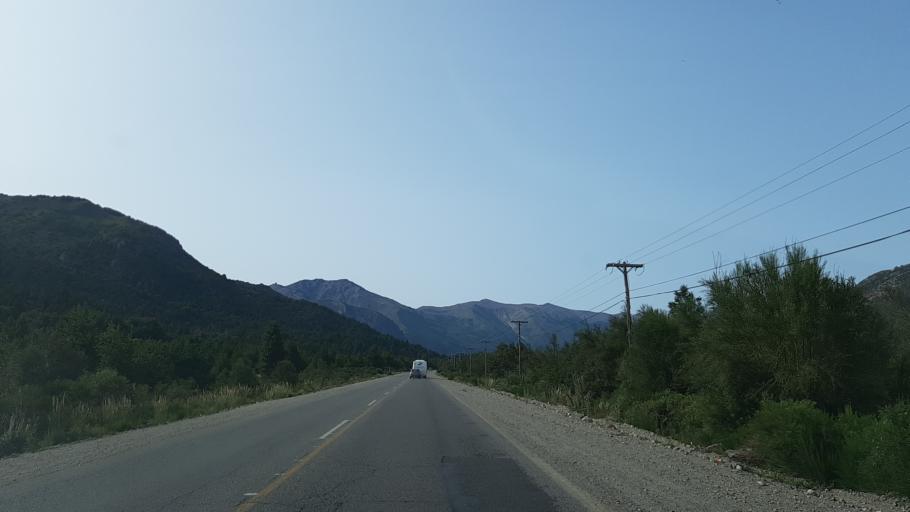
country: AR
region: Rio Negro
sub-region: Departamento de Bariloche
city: San Carlos de Bariloche
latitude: -41.1376
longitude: -71.4123
